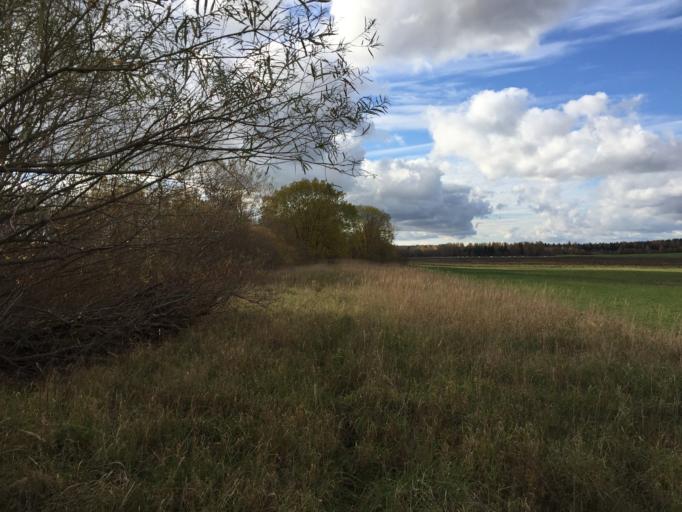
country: LV
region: Tukuma Rajons
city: Tukums
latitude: 56.9640
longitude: 23.0374
